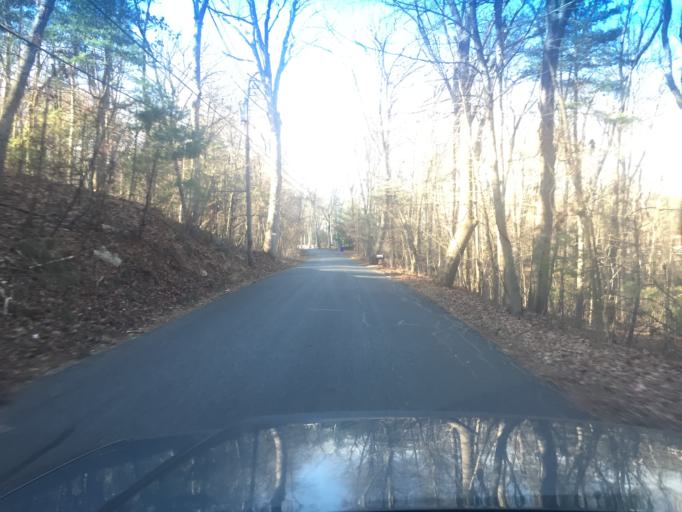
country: US
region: Massachusetts
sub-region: Middlesex County
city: Ashland
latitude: 42.2278
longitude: -71.4804
